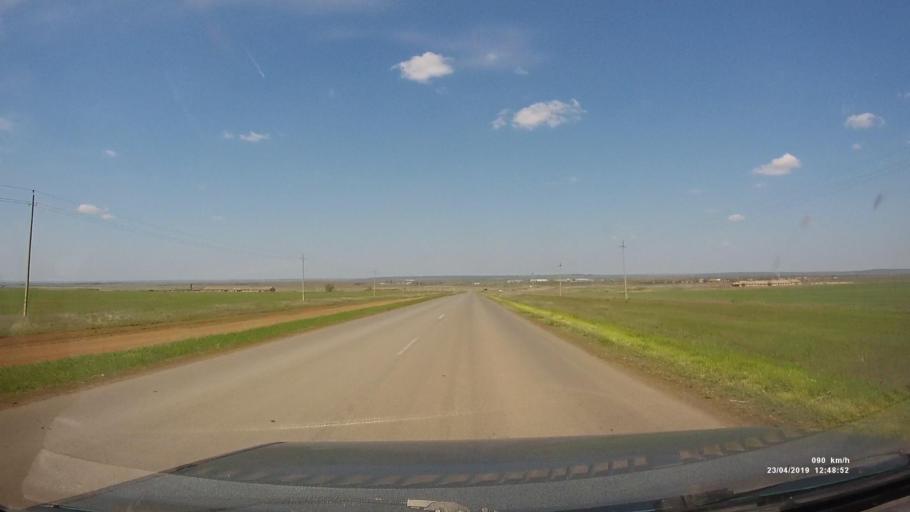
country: RU
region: Kalmykiya
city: Yashalta
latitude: 46.5299
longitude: 42.6389
